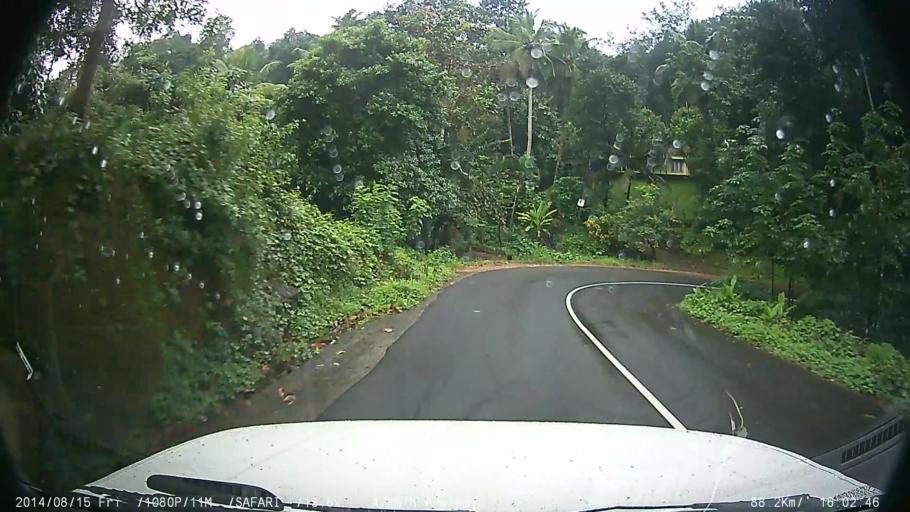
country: IN
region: Kerala
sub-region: Kottayam
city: Lalam
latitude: 9.7686
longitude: 76.7084
